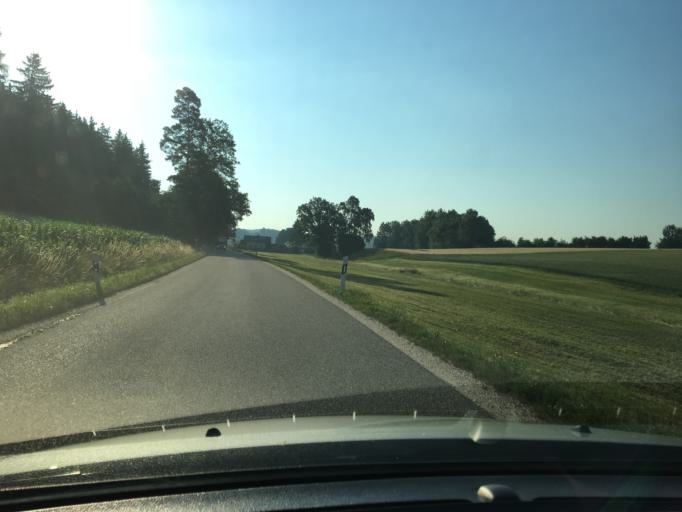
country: DE
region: Bavaria
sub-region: Lower Bavaria
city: Vilsbiburg
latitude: 48.4384
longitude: 12.3310
